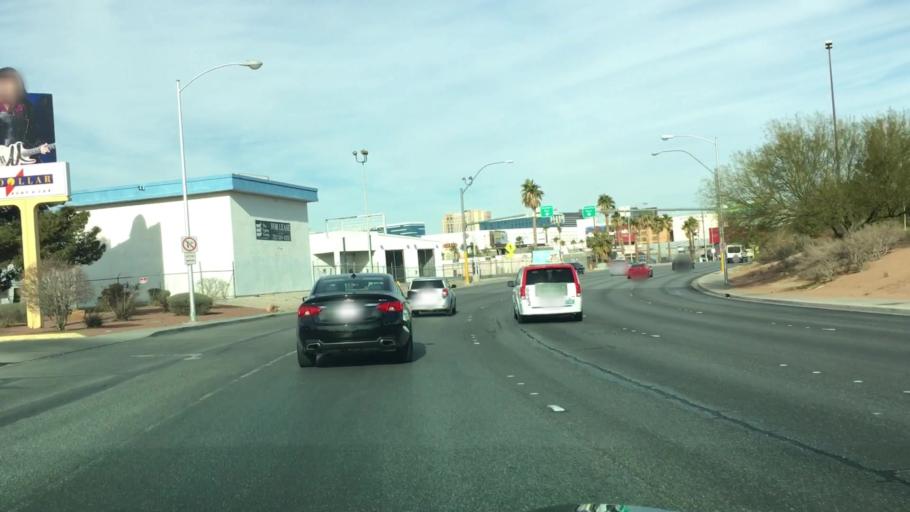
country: US
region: Nevada
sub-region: Clark County
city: Paradise
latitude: 36.1036
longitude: -115.1491
